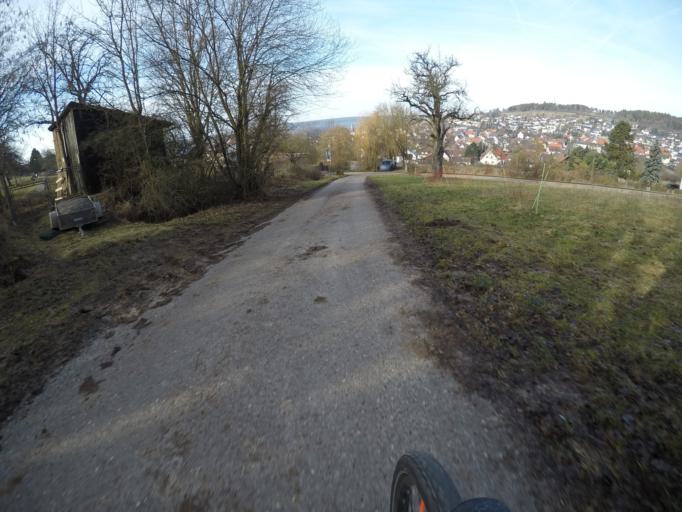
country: DE
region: Baden-Wuerttemberg
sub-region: Karlsruhe Region
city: Althengstett
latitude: 48.6930
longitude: 8.7784
